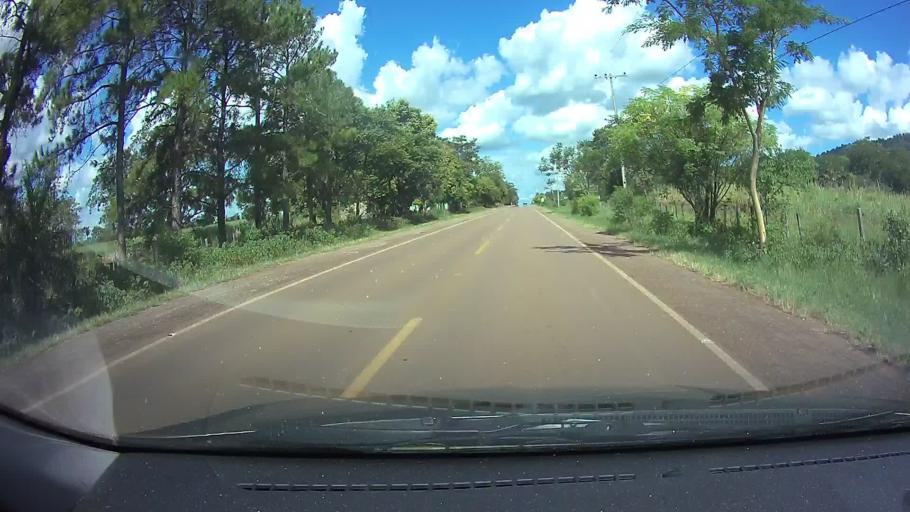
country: PY
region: Paraguari
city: La Colmena
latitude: -25.9131
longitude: -56.7499
